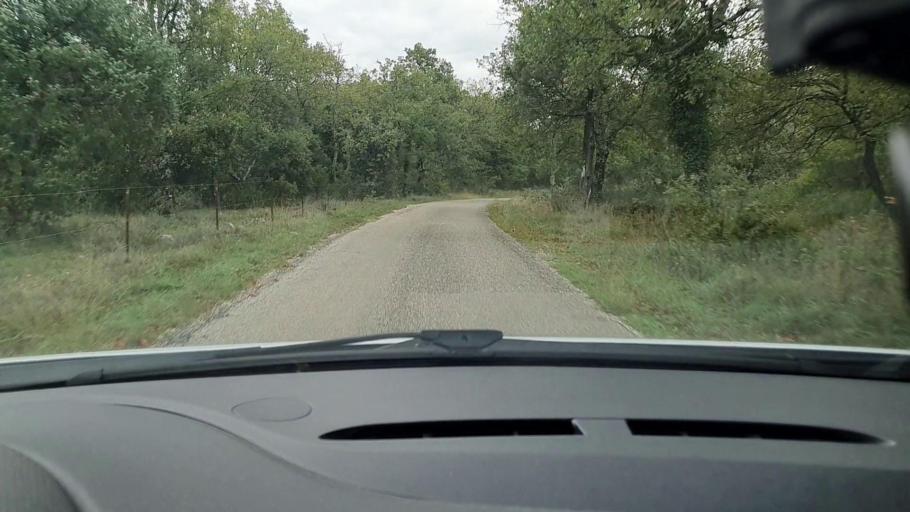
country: FR
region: Languedoc-Roussillon
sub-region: Departement du Gard
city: Mons
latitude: 44.1552
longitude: 4.2905
